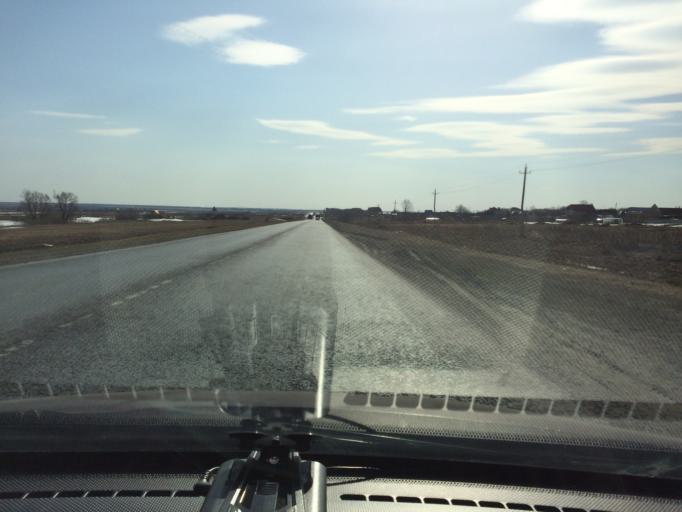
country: RU
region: Mariy-El
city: Yoshkar-Ola
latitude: 56.7150
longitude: 48.0930
